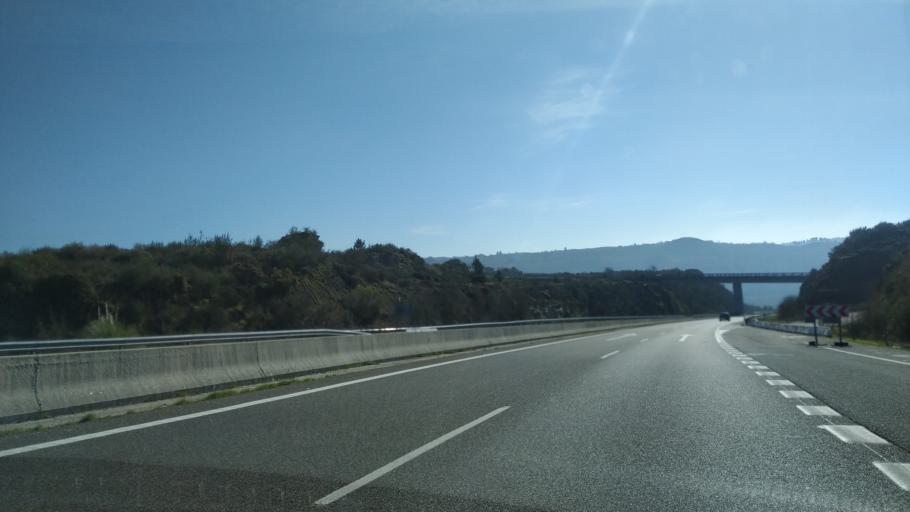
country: ES
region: Galicia
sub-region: Provincia de Ourense
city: Punxin
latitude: 42.3967
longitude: -8.0001
